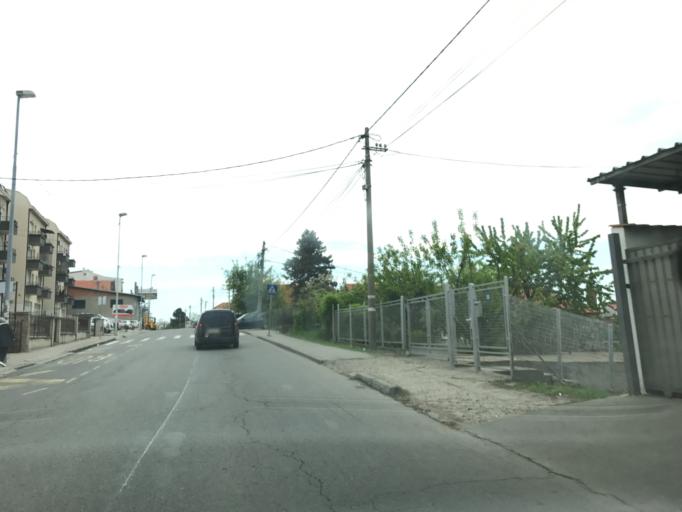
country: RS
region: Central Serbia
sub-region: Belgrade
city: Palilula
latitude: 44.8018
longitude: 20.5196
